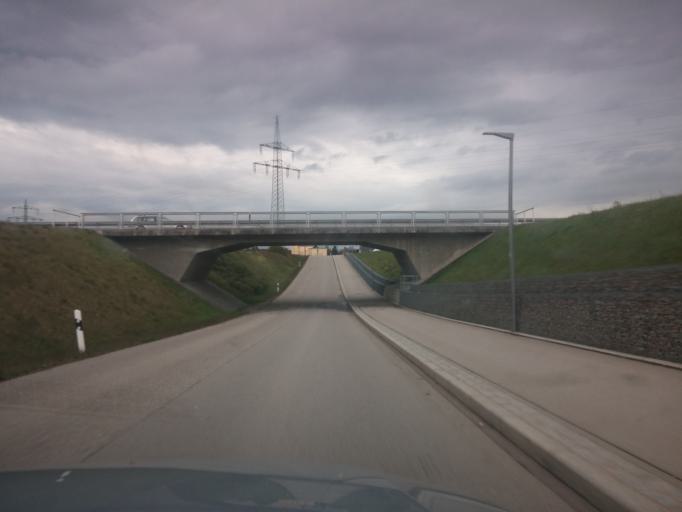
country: DE
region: Bavaria
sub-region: Upper Bavaria
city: Putzbrunn
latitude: 48.0838
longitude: 11.7139
